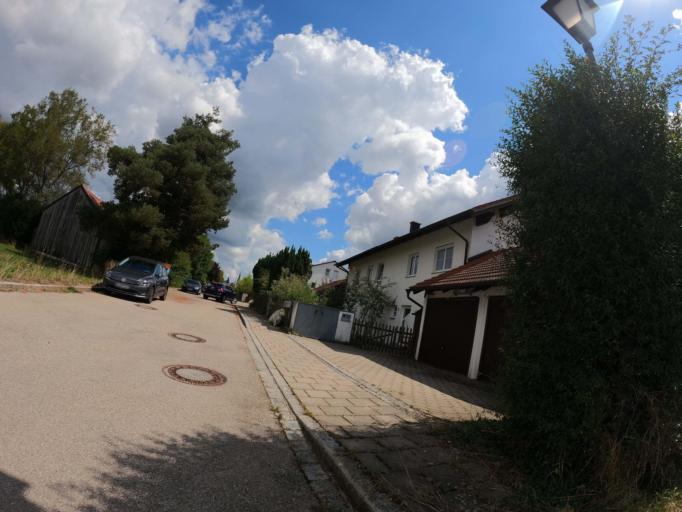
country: DE
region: Bavaria
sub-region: Upper Bavaria
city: Brunnthal
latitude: 48.0057
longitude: 11.6783
